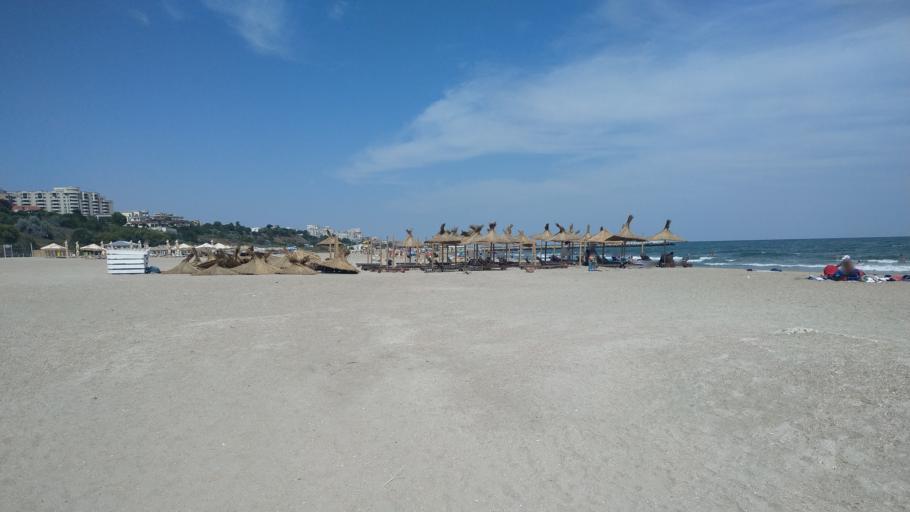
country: RO
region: Constanta
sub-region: Municipiul Constanta
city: Constanta
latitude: 44.1838
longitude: 28.6560
